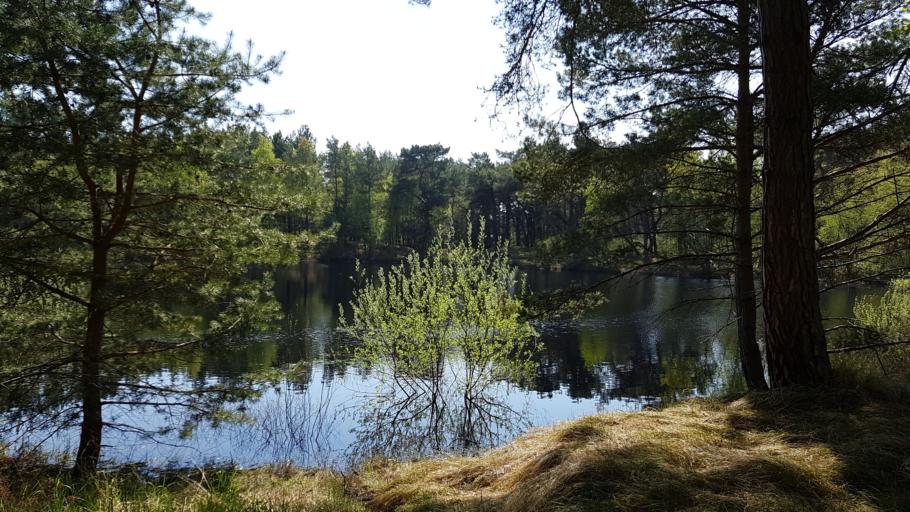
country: DK
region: Capital Region
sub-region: Bornholm Kommune
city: Nexo
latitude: 54.9995
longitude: 15.0890
